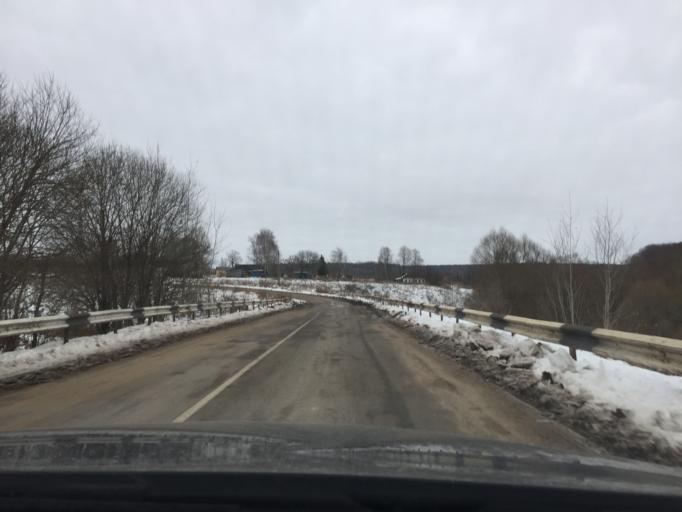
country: RU
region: Tula
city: Teploye
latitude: 53.7730
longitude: 37.6434
